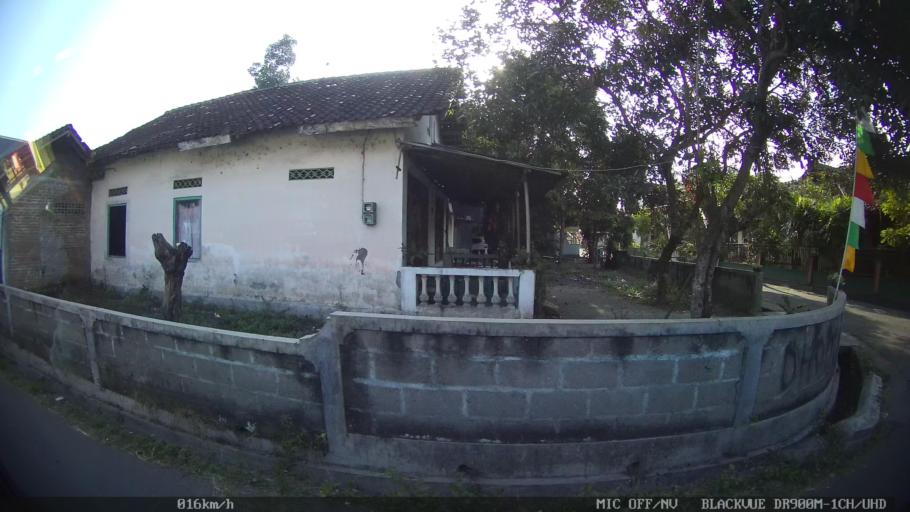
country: ID
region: Daerah Istimewa Yogyakarta
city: Gamping Lor
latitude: -7.7953
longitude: 110.3330
